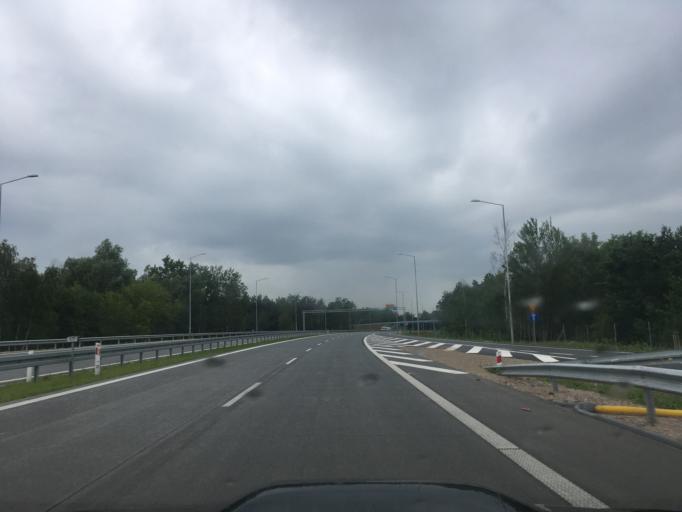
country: PL
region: Masovian Voivodeship
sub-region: Powiat piaseczynski
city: Gora Kalwaria
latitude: 51.9695
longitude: 21.2083
